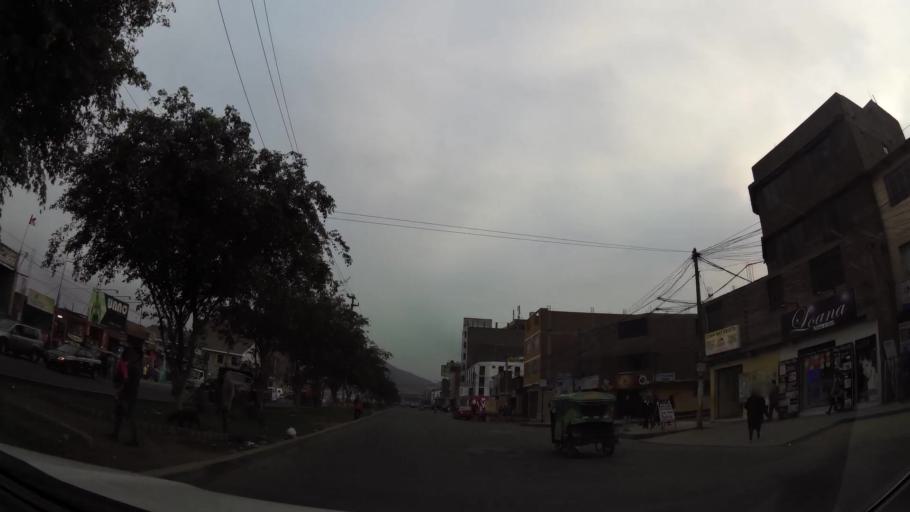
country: PE
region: Lima
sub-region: Lima
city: Independencia
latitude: -12.0042
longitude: -77.0029
